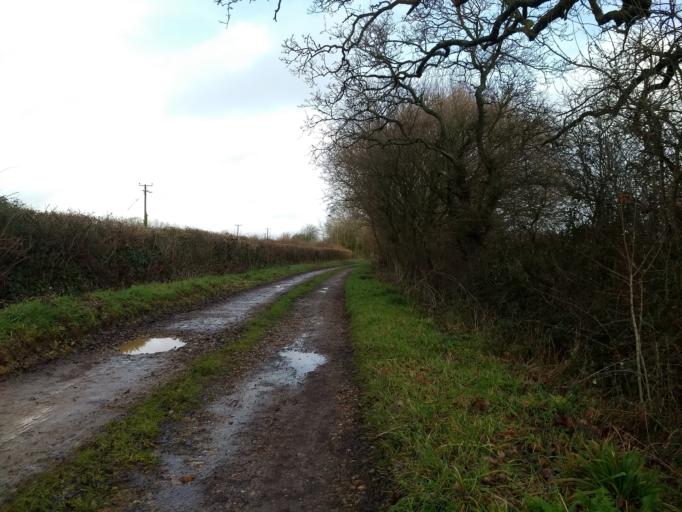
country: GB
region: England
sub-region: Isle of Wight
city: Newport
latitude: 50.7109
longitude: -1.2417
